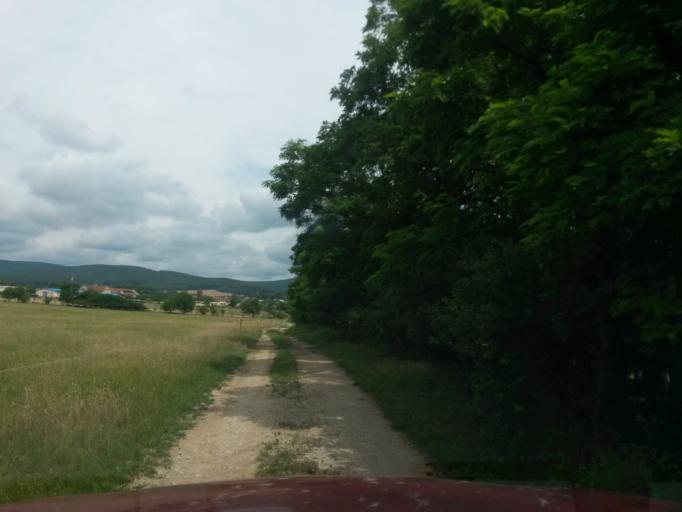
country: SK
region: Kosicky
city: Moldava nad Bodvou
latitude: 48.6663
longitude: 21.1123
